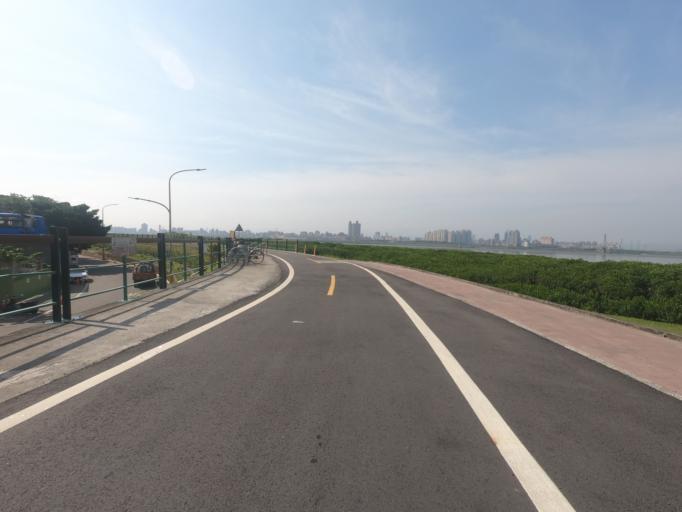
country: TW
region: Taipei
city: Taipei
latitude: 25.1091
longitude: 121.4662
